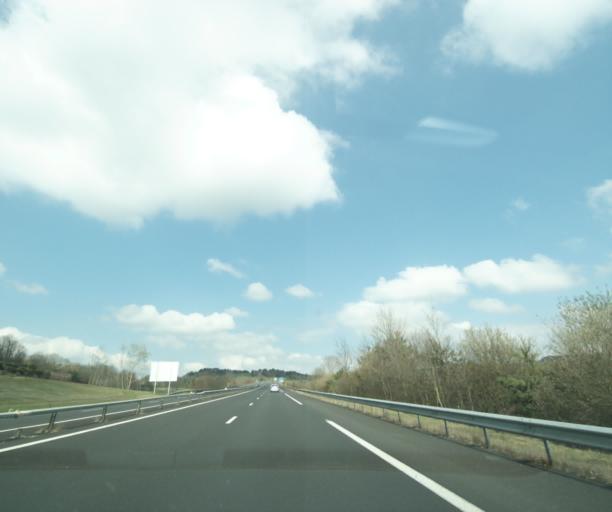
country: FR
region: Auvergne
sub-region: Departement du Cantal
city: Saint-Flour
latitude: 45.0762
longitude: 3.1163
